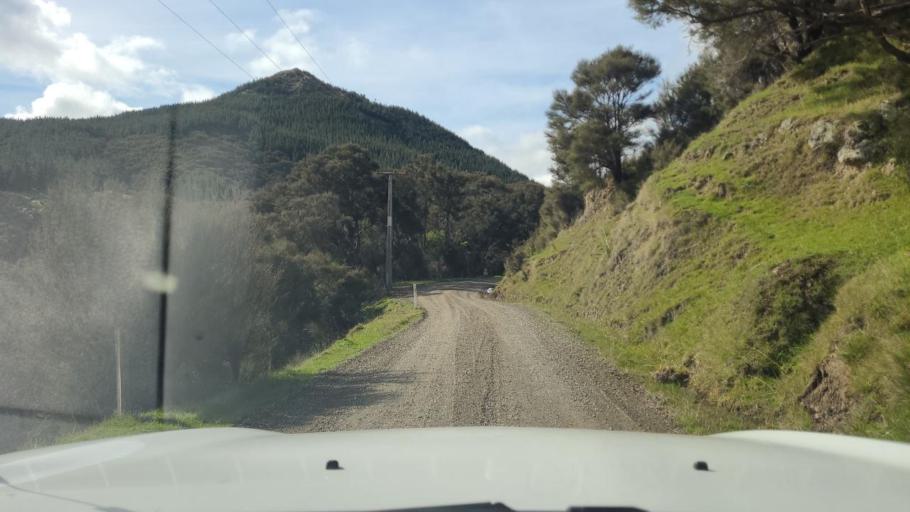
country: NZ
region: Wellington
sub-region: South Wairarapa District
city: Waipawa
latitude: -41.3401
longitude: 175.6693
